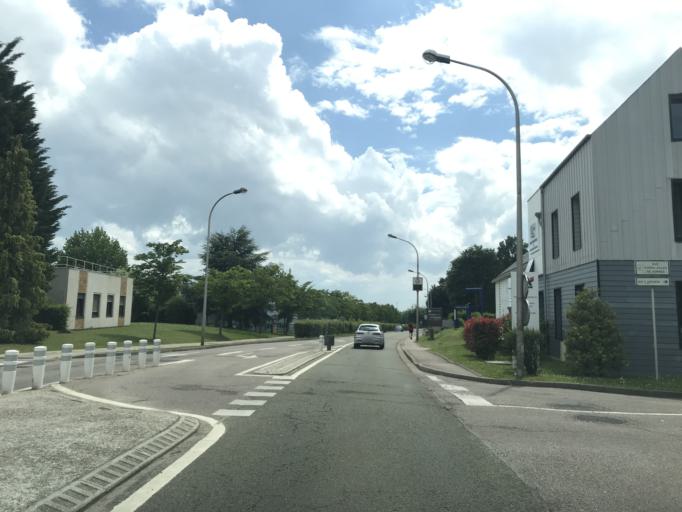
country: FR
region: Haute-Normandie
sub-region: Departement de la Seine-Maritime
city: Mont-Saint-Aignan
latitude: 49.4739
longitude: 1.0926
